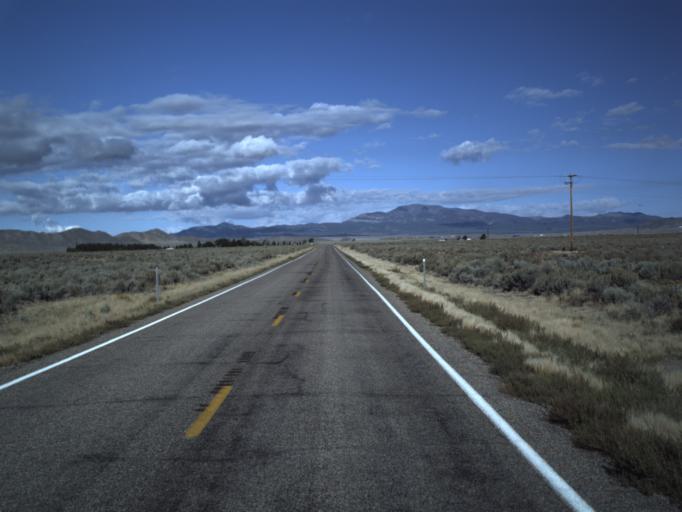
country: US
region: Utah
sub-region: Beaver County
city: Milford
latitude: 38.4011
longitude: -113.0363
